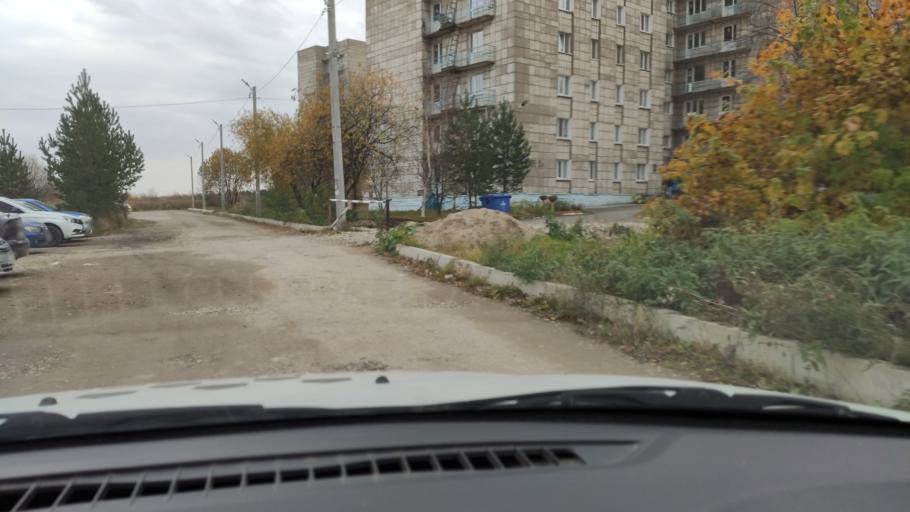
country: RU
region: Perm
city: Froly
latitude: 57.9555
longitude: 56.2744
